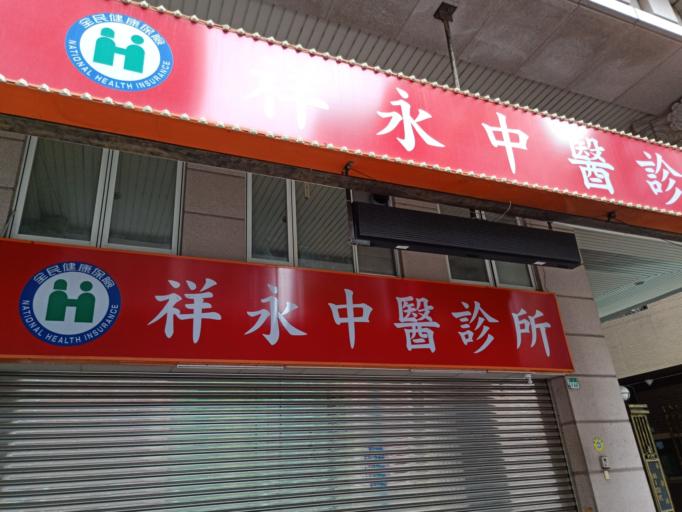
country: TW
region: Taipei
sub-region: Taipei
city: Banqiao
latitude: 25.0847
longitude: 121.4610
